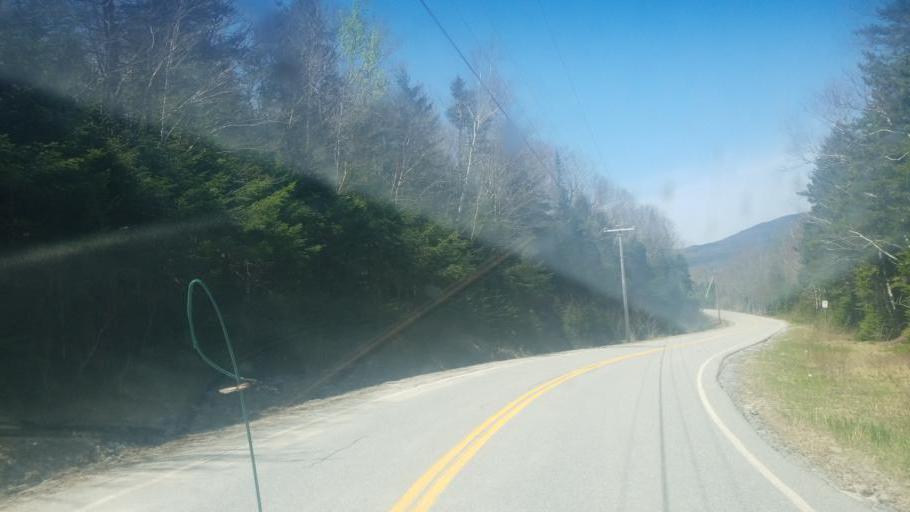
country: US
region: New Hampshire
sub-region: Coos County
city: Jefferson
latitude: 44.2672
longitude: -71.3565
